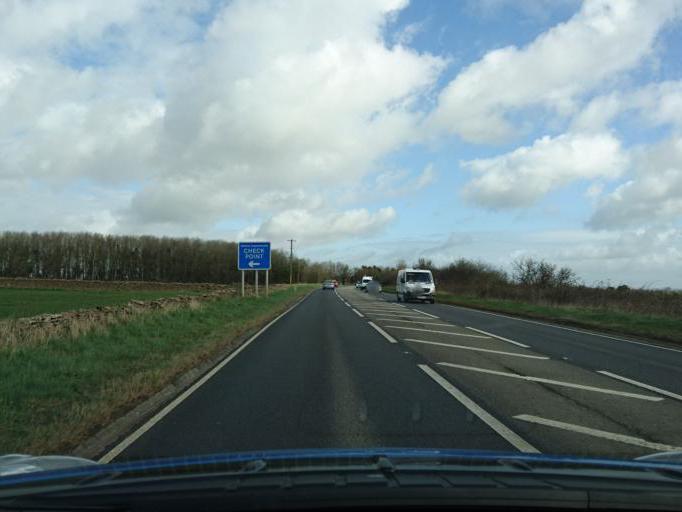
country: GB
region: England
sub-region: South Gloucestershire
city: Hinton
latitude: 51.4949
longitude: -2.3548
